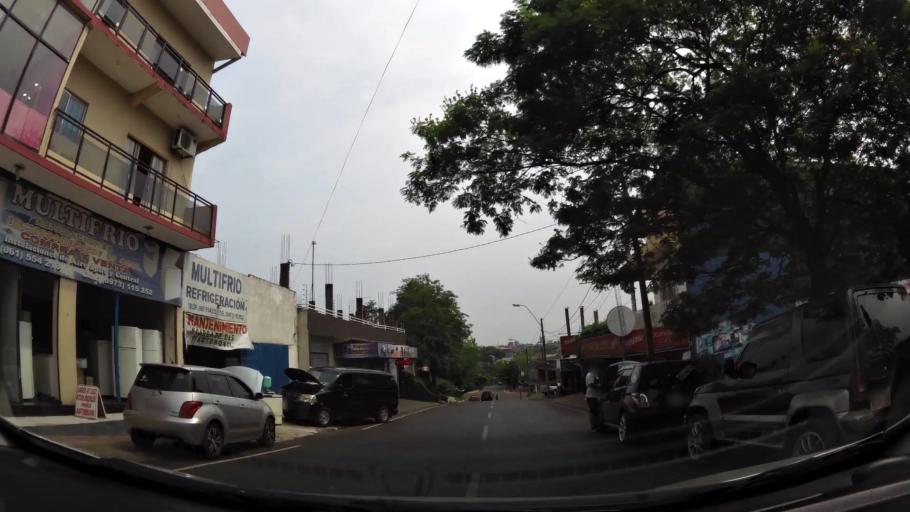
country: BR
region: Parana
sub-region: Foz Do Iguacu
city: Foz do Iguacu
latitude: -25.5507
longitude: -54.6069
